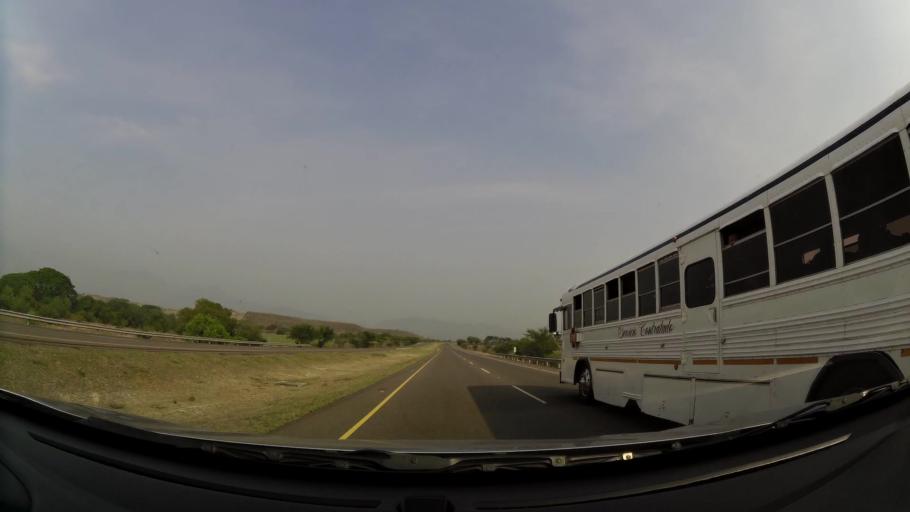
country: HN
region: Comayagua
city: Comayagua
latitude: 14.4335
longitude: -87.6505
